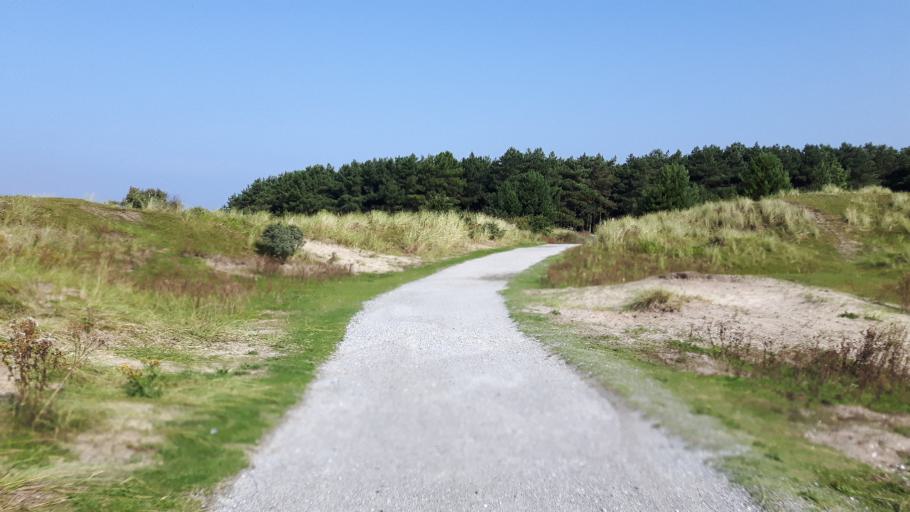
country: NL
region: Friesland
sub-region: Gemeente Ameland
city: Nes
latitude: 53.4580
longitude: 5.8147
